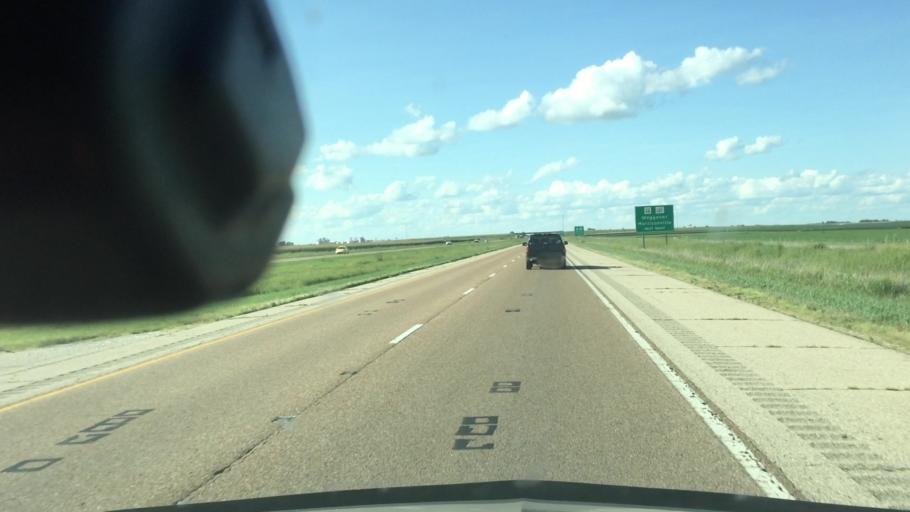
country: US
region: Illinois
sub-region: Montgomery County
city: Raymond
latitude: 39.3077
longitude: -89.6422
